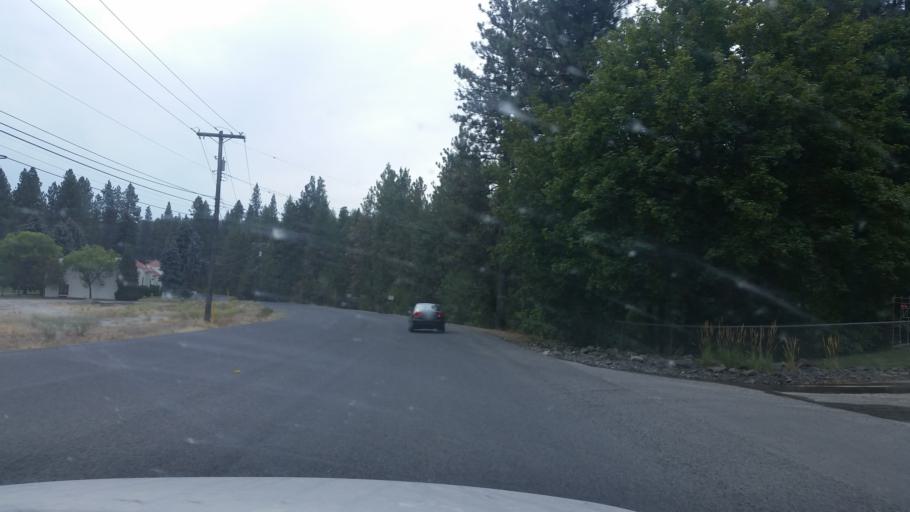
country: US
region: Washington
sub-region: Spokane County
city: Spokane
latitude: 47.6643
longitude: -117.4689
